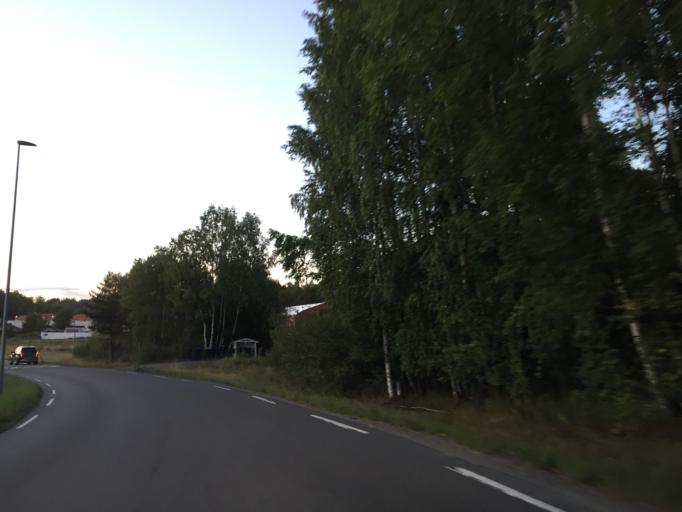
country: NO
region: Ostfold
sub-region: Moss
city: Moss
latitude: 59.4910
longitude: 10.6917
